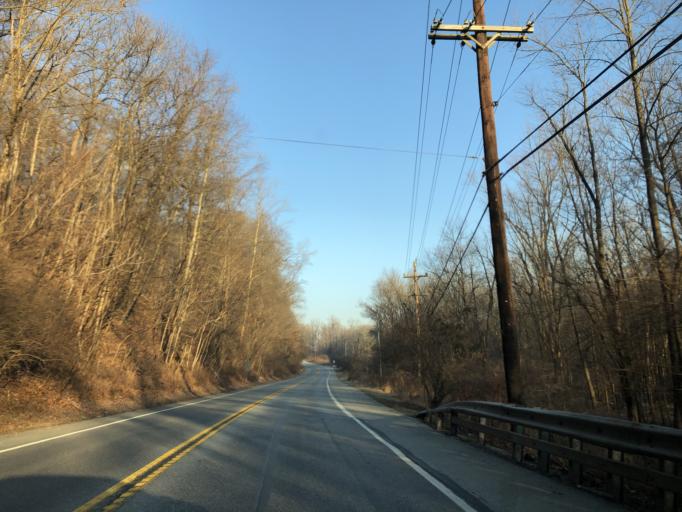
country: US
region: Pennsylvania
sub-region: Chester County
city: Downingtown
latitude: 39.9823
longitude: -75.6882
